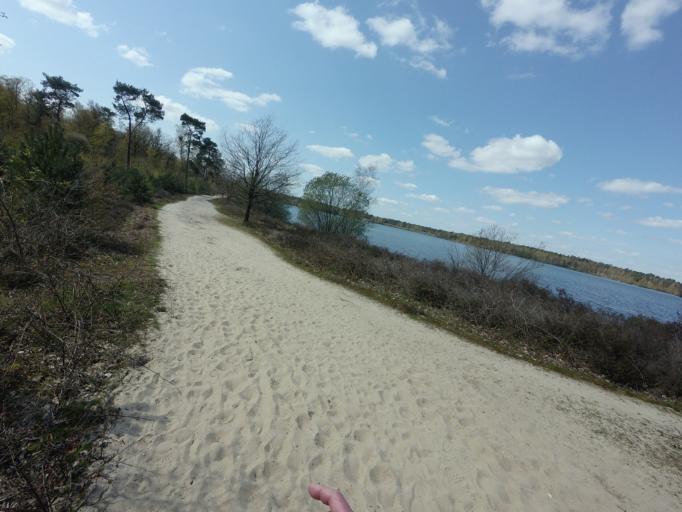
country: NL
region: Limburg
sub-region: Gemeente Bergen
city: Wellerlooi
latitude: 51.5716
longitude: 6.1057
